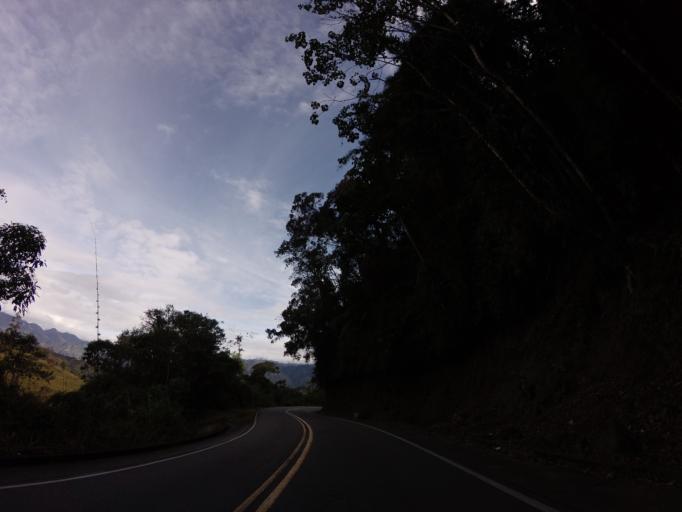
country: CO
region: Tolima
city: Herveo
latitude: 5.1434
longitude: -75.1542
